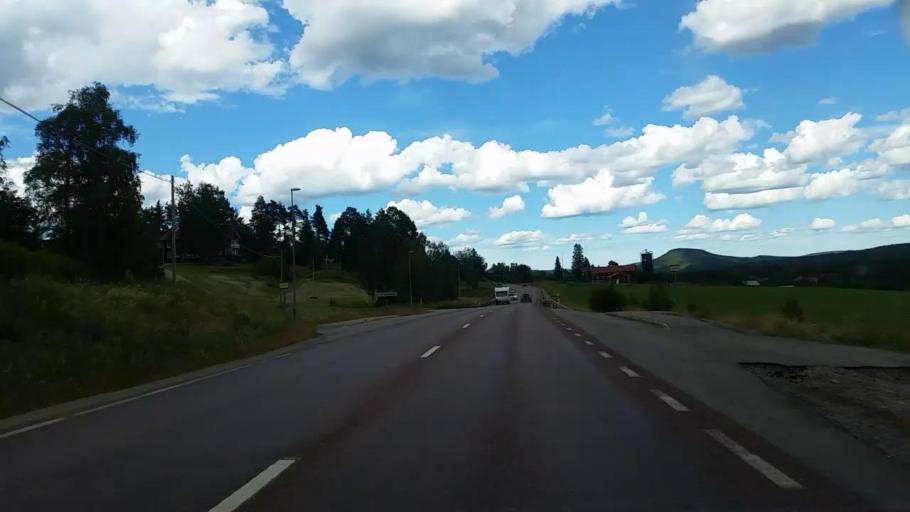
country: SE
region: Gaevleborg
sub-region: Ljusdals Kommun
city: Jaervsoe
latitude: 61.6950
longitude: 16.1570
